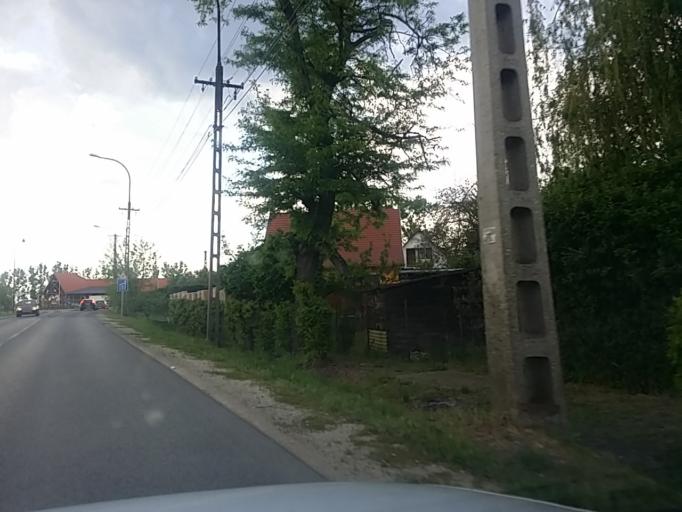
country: HU
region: Pest
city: Veresegyhaz
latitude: 47.6572
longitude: 19.2723
